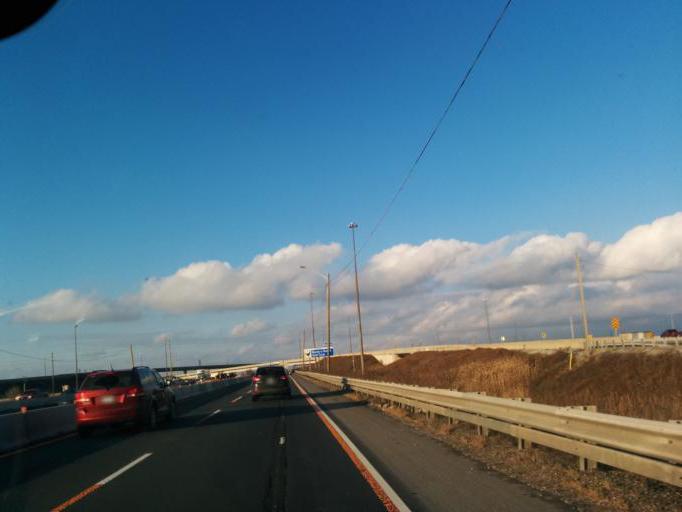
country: CA
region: Ontario
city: Etobicoke
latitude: 43.7497
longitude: -79.6303
